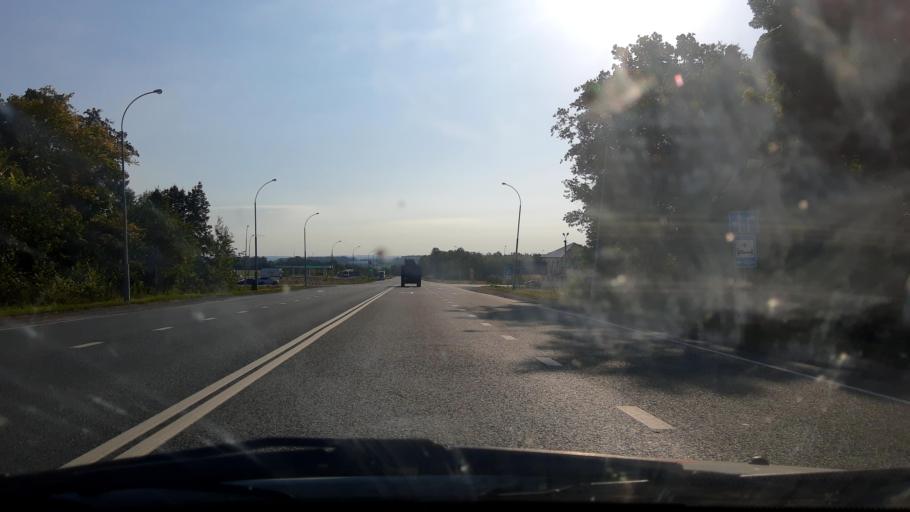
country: RU
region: Bashkortostan
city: Oktyabr'skiy
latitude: 54.4477
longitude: 53.5862
